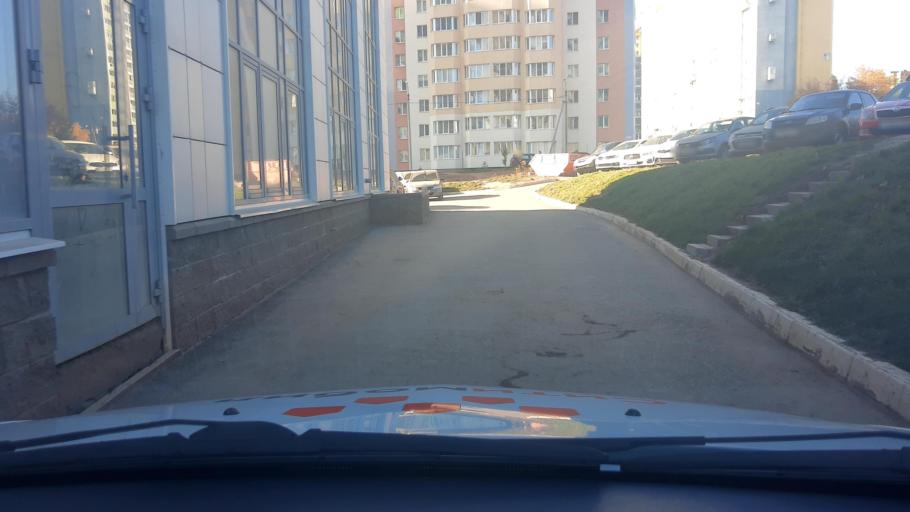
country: RU
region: Bashkortostan
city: Ufa
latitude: 54.7660
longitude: 56.0323
